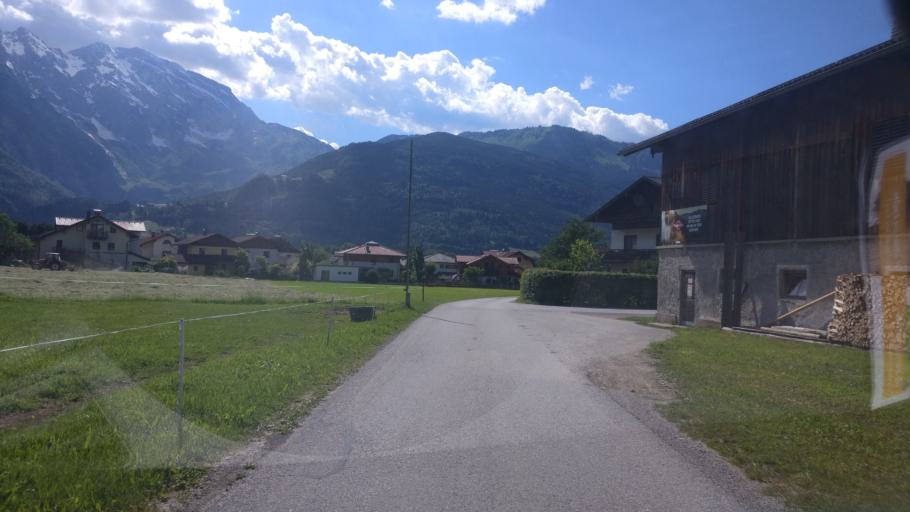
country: AT
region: Salzburg
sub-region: Politischer Bezirk Hallein
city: Golling an der Salzach
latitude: 47.6182
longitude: 13.1649
